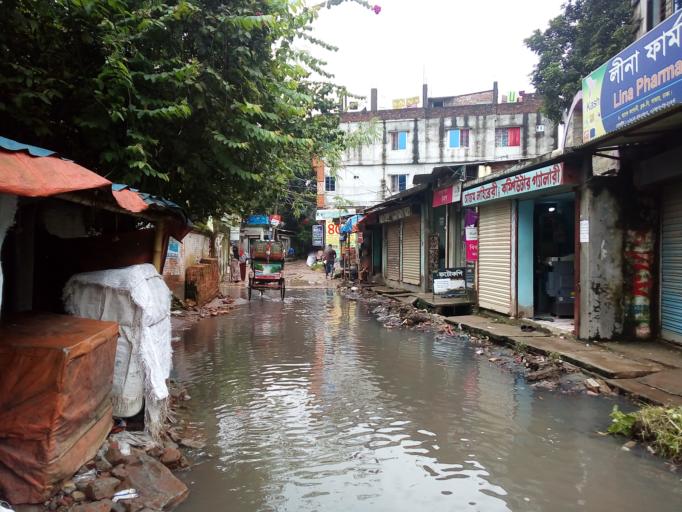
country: BD
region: Dhaka
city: Tungi
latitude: 23.8421
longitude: 90.2514
